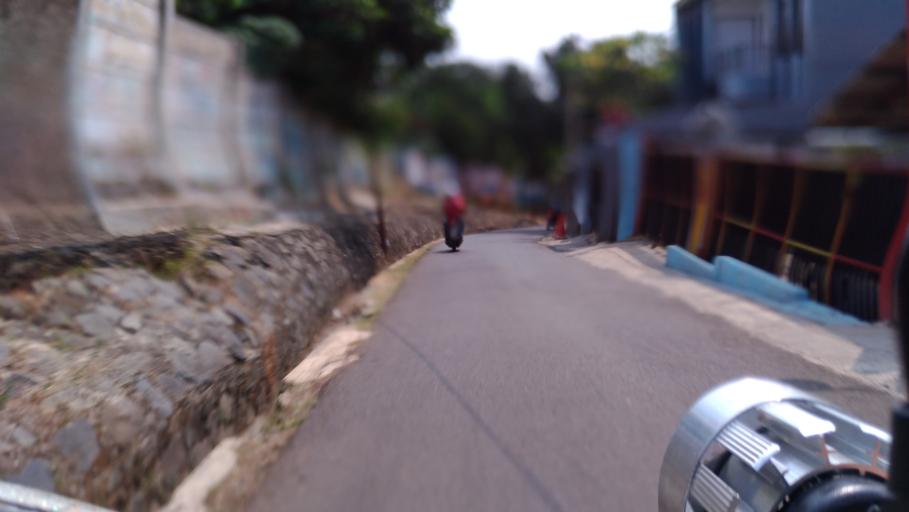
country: ID
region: West Java
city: Cileungsir
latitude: -6.3544
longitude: 106.8969
